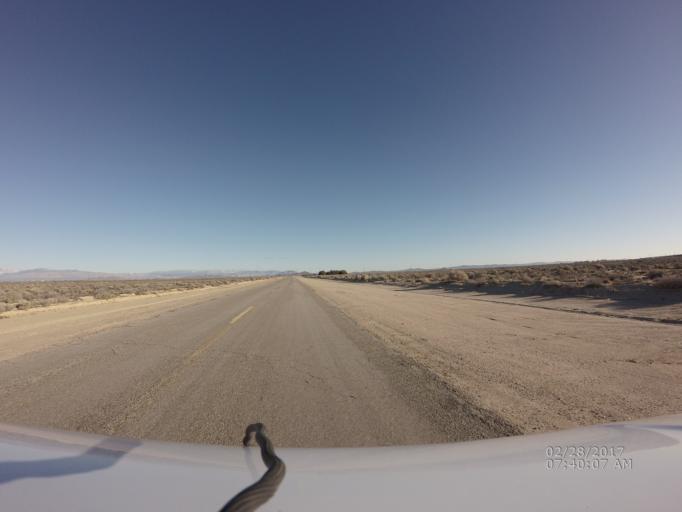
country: US
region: California
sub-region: Los Angeles County
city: Lancaster
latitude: 34.7725
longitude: -118.1845
